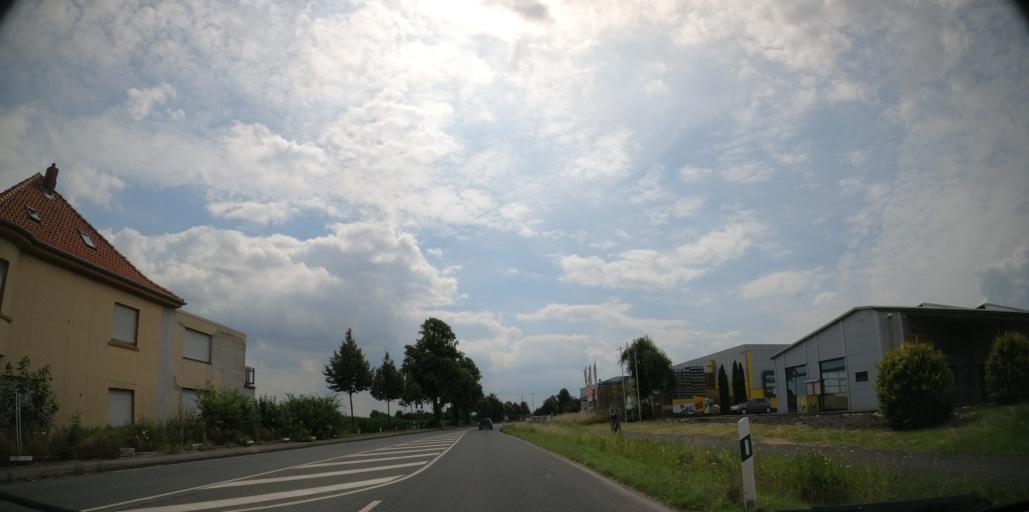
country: DE
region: North Rhine-Westphalia
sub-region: Regierungsbezirk Arnsberg
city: Lippstadt
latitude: 51.6608
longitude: 8.3637
